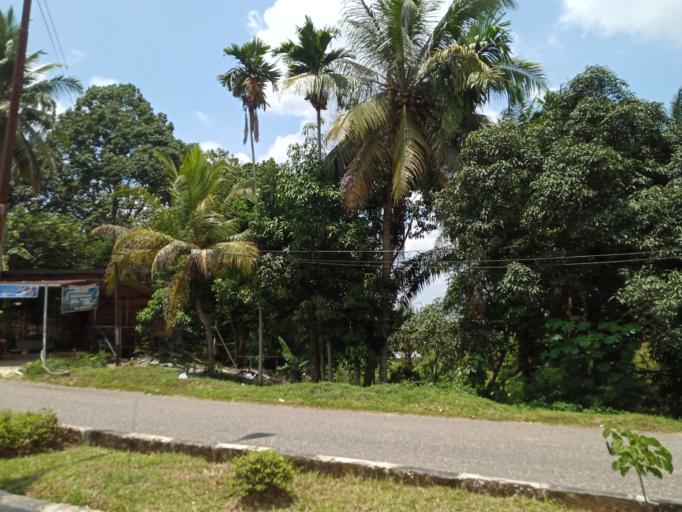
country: ID
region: Jambi
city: Bangko
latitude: -2.0566
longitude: 102.2801
